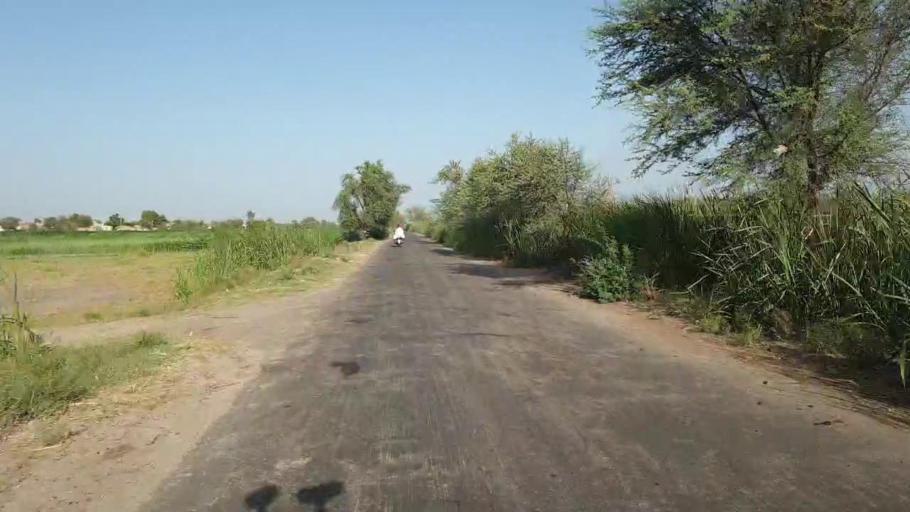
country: PK
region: Sindh
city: Nawabshah
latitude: 26.3745
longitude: 68.4667
